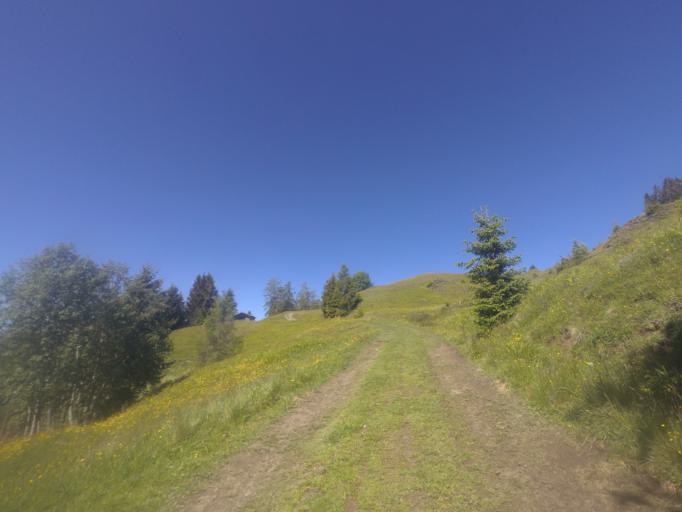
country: AT
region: Salzburg
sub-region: Politischer Bezirk Zell am See
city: Lend
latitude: 47.3240
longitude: 13.0433
